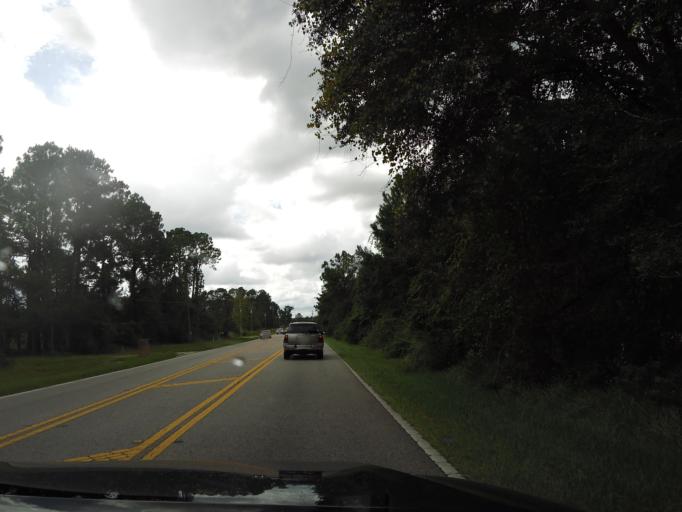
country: US
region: Florida
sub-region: Clay County
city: Lakeside
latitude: 30.1009
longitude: -81.8064
